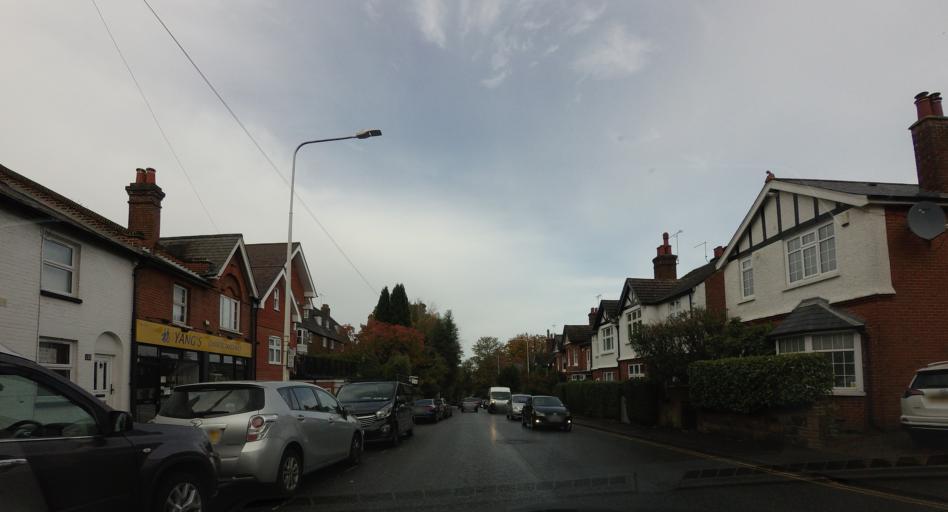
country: GB
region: England
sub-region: Kent
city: Sevenoaks
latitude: 51.2748
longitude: 0.1876
